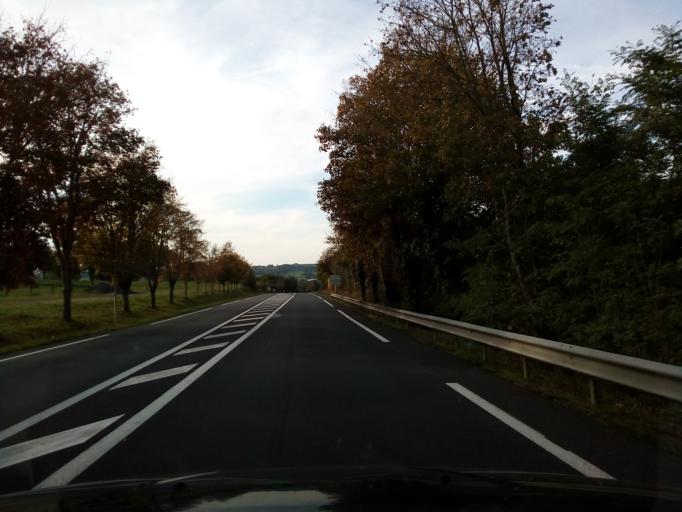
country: FR
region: Poitou-Charentes
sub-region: Departement de la Charente
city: Confolens
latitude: 46.0629
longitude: 0.6943
